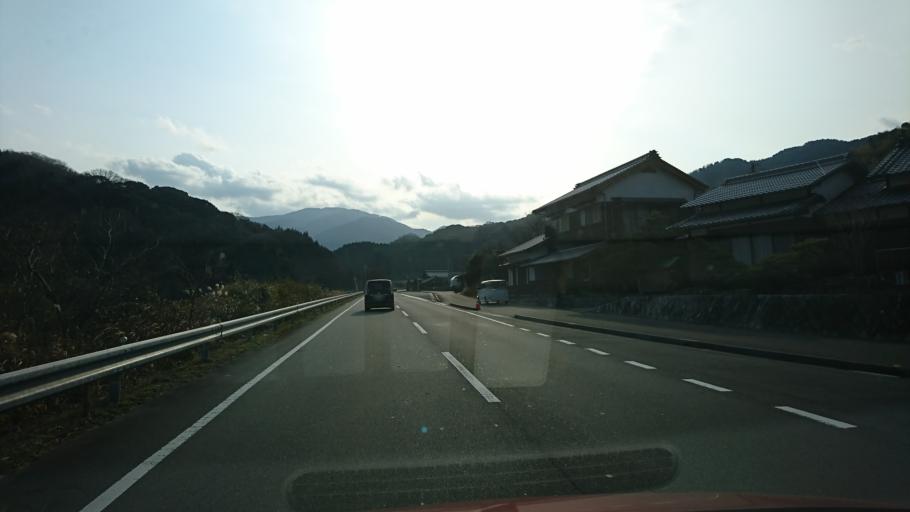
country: JP
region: Ehime
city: Hojo
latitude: 33.9899
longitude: 132.9118
